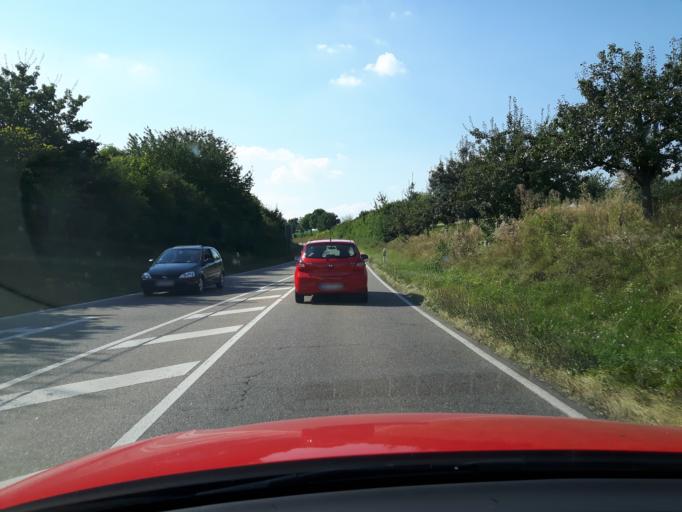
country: DE
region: Baden-Wuerttemberg
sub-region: Regierungsbezirk Stuttgart
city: Nordheim
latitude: 49.1125
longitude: 9.1405
